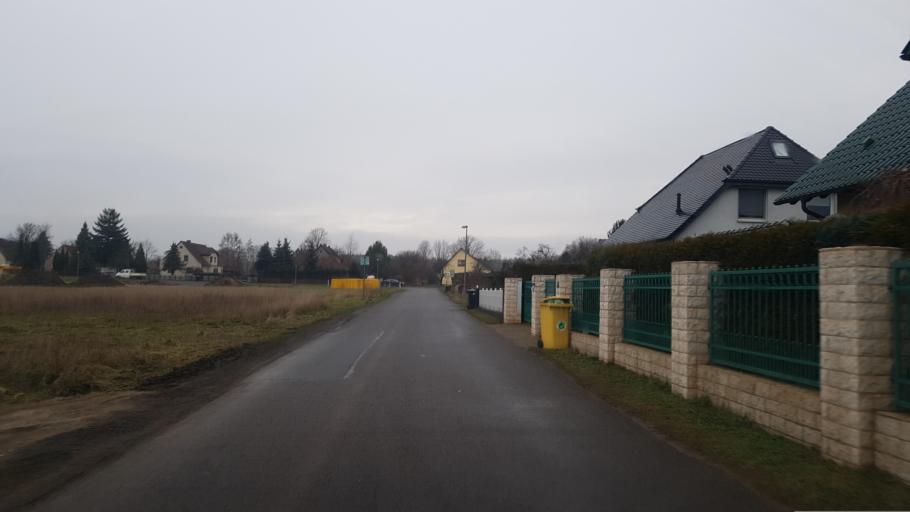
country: DE
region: Brandenburg
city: Drebkau
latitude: 51.6891
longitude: 14.2798
